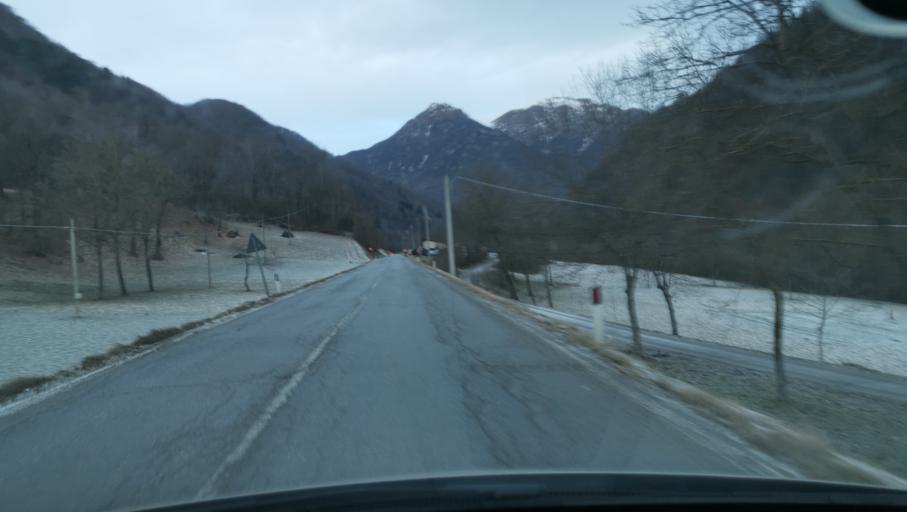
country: IT
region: Piedmont
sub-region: Provincia di Cuneo
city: Monterosso Grana
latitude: 44.4091
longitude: 7.3043
